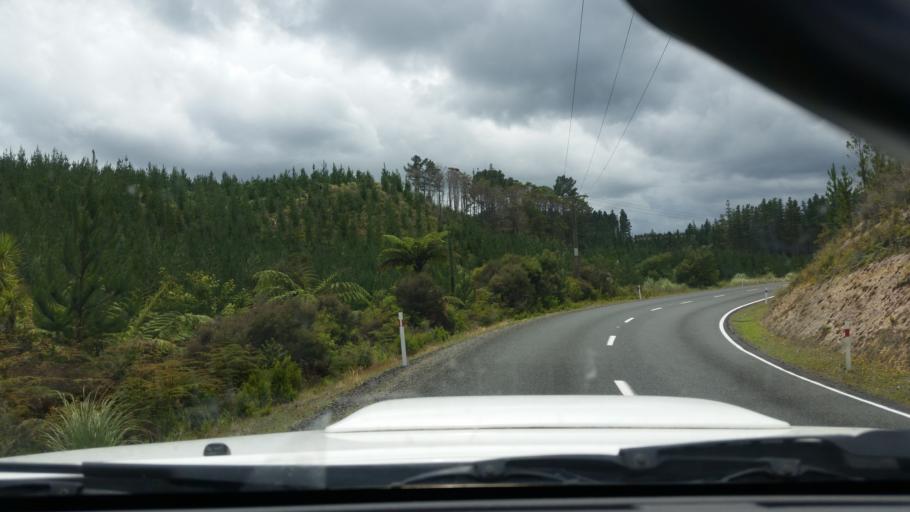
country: NZ
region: Northland
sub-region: Kaipara District
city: Dargaville
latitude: -35.8188
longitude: 173.7109
